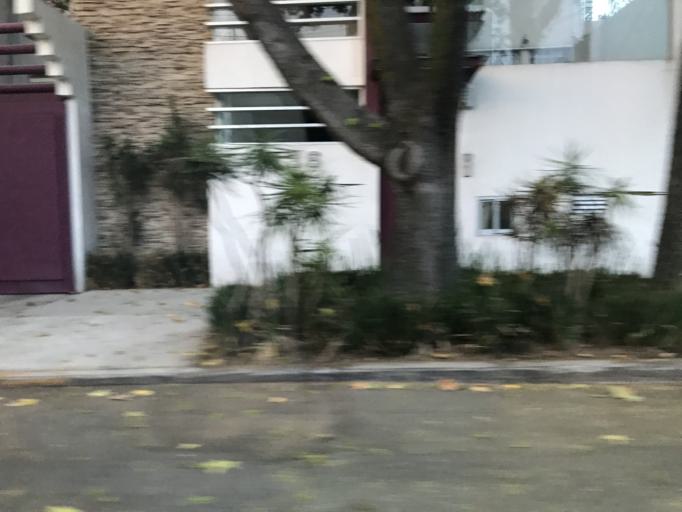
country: MX
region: Mexico City
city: Benito Juarez
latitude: 19.3991
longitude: -99.1579
